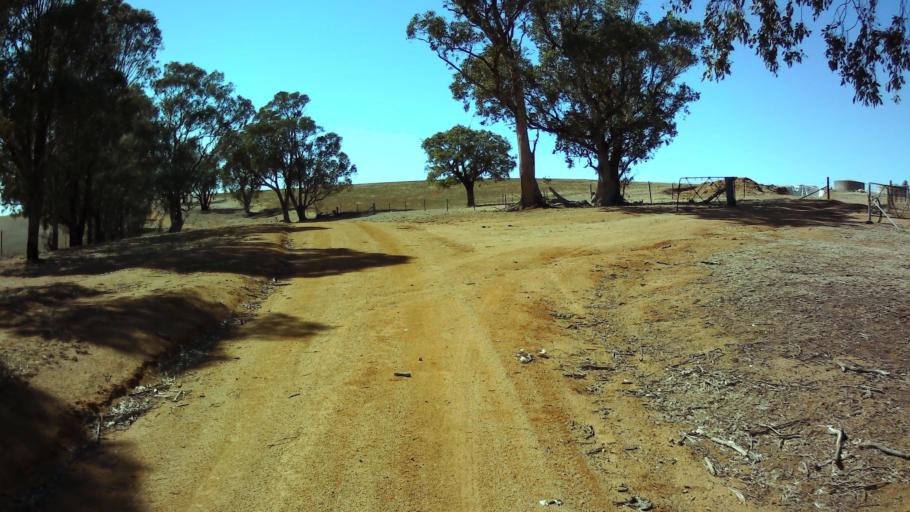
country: AU
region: New South Wales
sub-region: Cowra
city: Cowra
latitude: -33.9744
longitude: 148.4627
